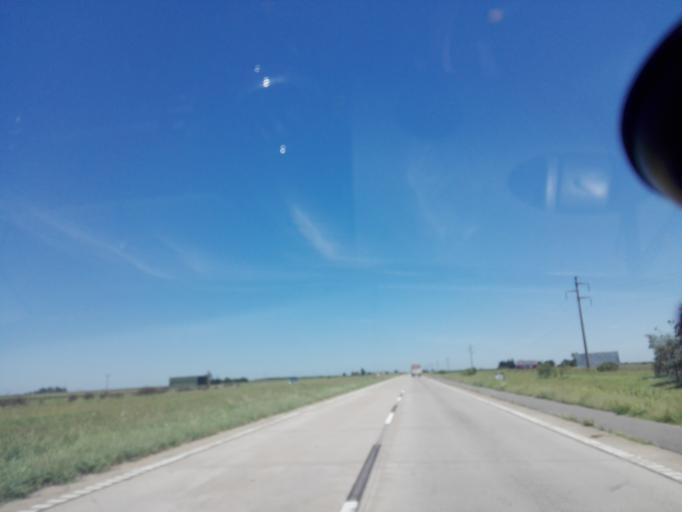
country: AR
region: Santa Fe
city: Canada de Gomez
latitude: -32.8609
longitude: -61.3063
